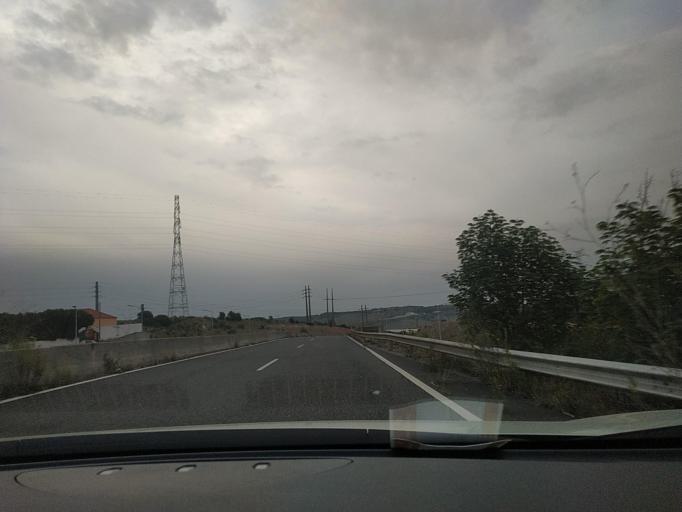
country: PT
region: Lisbon
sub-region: Loures
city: Santo Antao do Tojal
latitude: 38.8640
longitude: -9.1337
